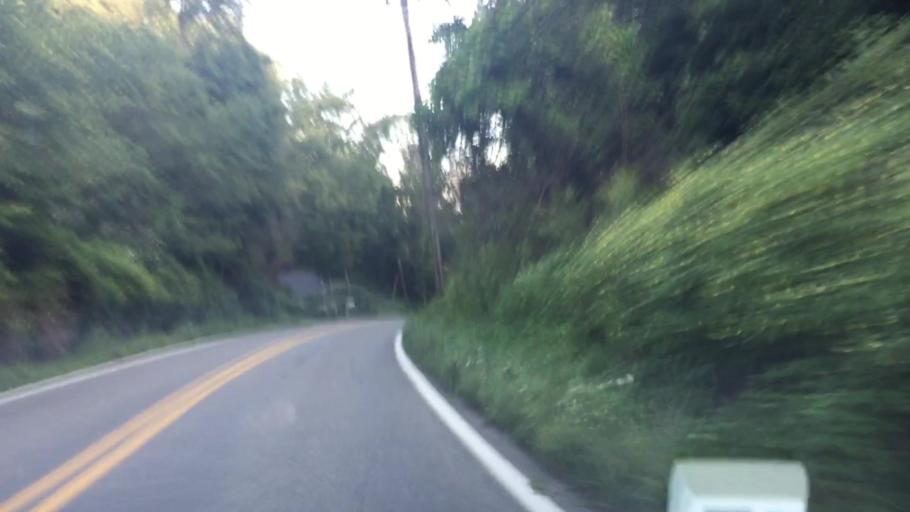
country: US
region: Pennsylvania
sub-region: Beaver County
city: Ambridge
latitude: 40.5696
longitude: -80.2666
